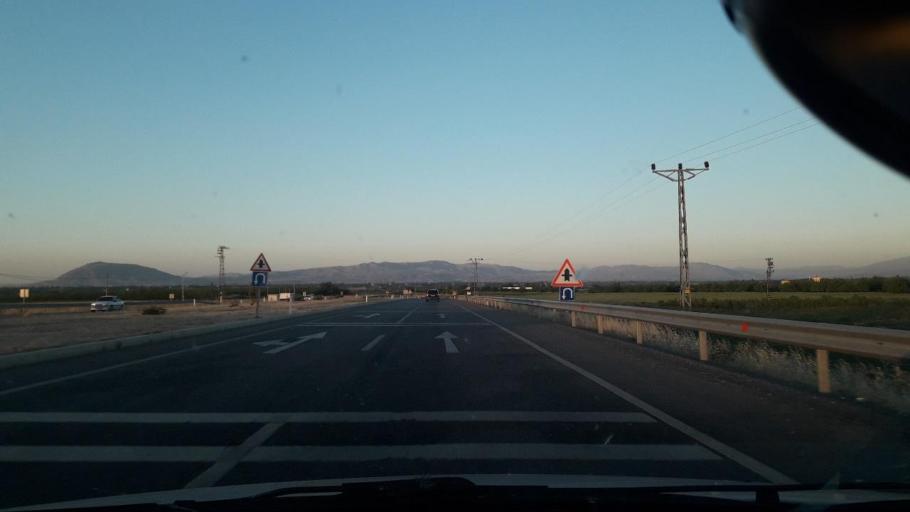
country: TR
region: Malatya
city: Yazihan
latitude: 38.4977
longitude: 38.2244
